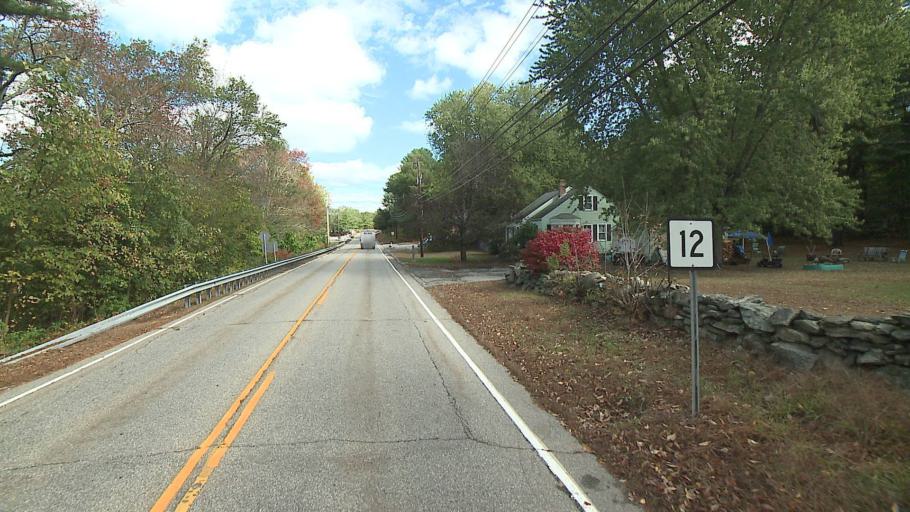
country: US
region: Connecticut
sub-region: Windham County
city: Killingly Center
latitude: 41.8698
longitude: -71.8799
